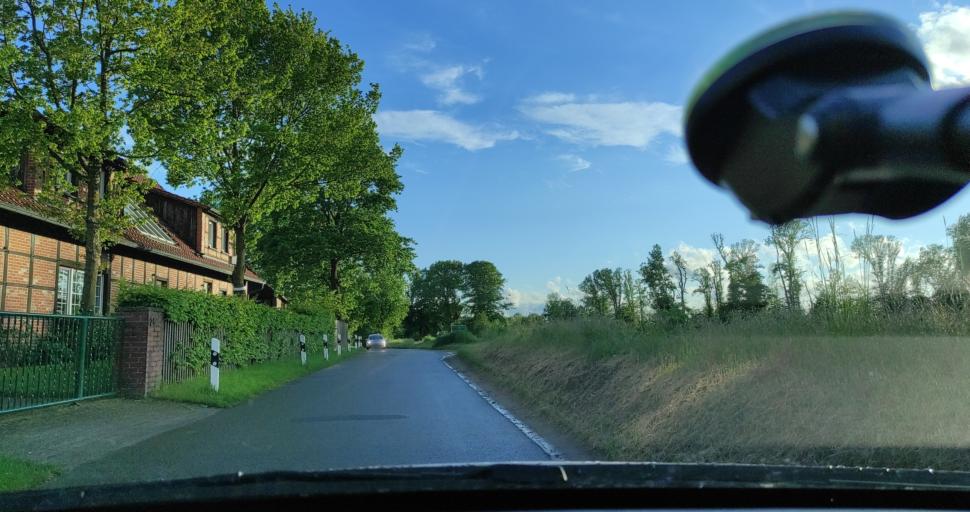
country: DE
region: North Rhine-Westphalia
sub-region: Regierungsbezirk Munster
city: Greven
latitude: 52.1009
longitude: 7.5766
